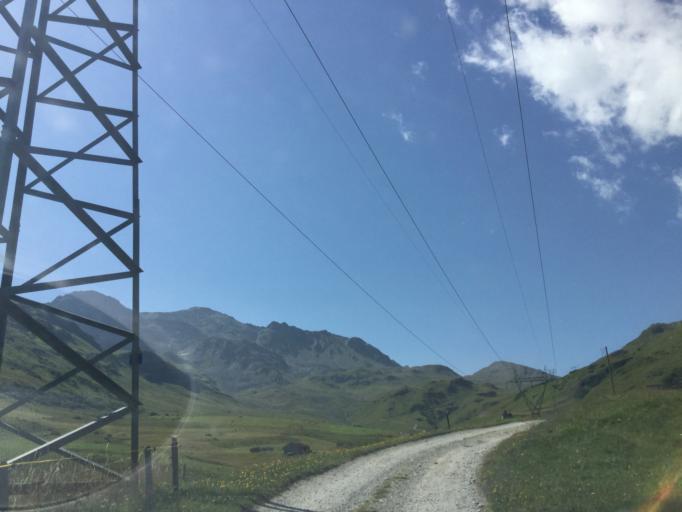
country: CH
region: Grisons
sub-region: Maloja District
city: Silvaplana
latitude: 46.4568
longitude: 9.6577
